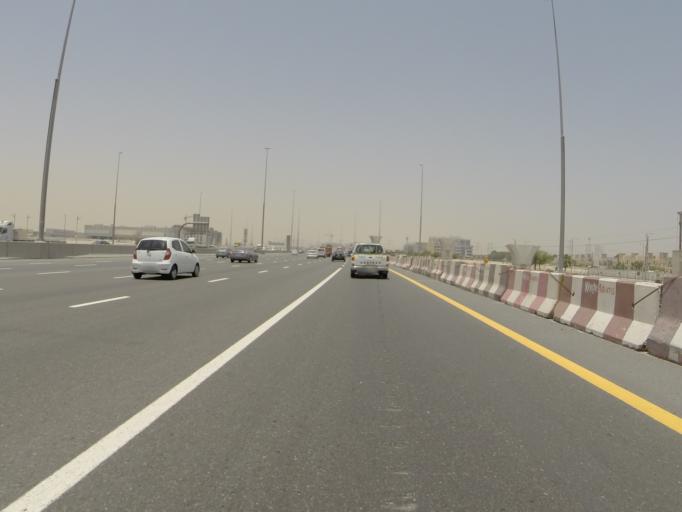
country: AE
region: Dubai
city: Dubai
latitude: 25.0412
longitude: 55.1891
